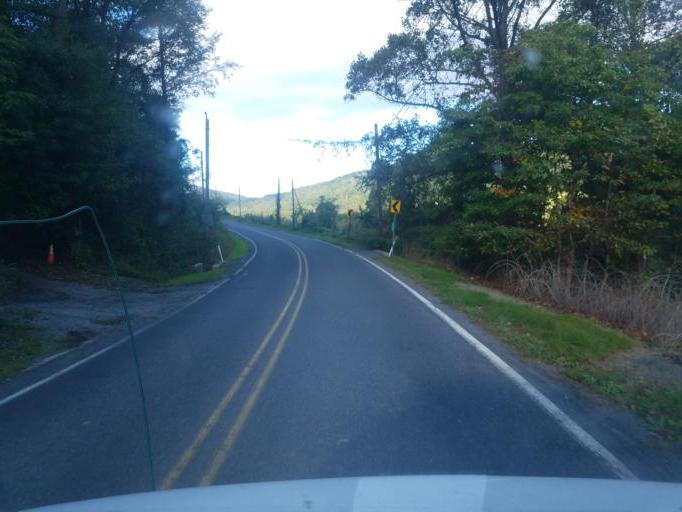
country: US
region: Pennsylvania
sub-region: Adams County
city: Biglerville
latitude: 39.8926
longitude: -77.3773
